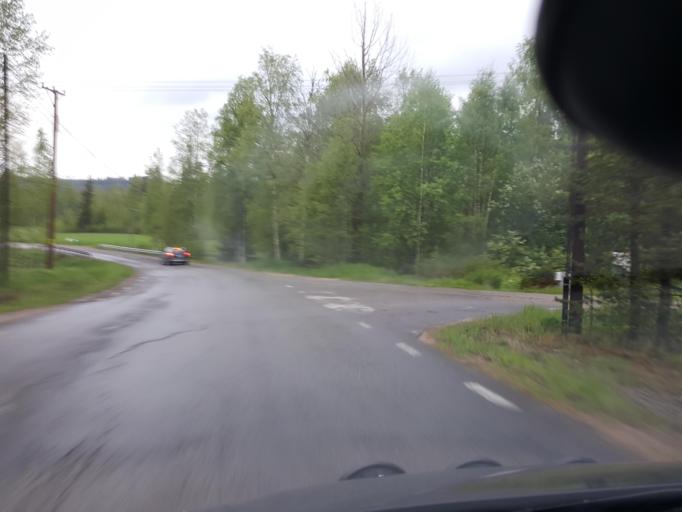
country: SE
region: Gaevleborg
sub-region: Ljusdals Kommun
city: Jaervsoe
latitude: 61.7884
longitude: 16.2177
